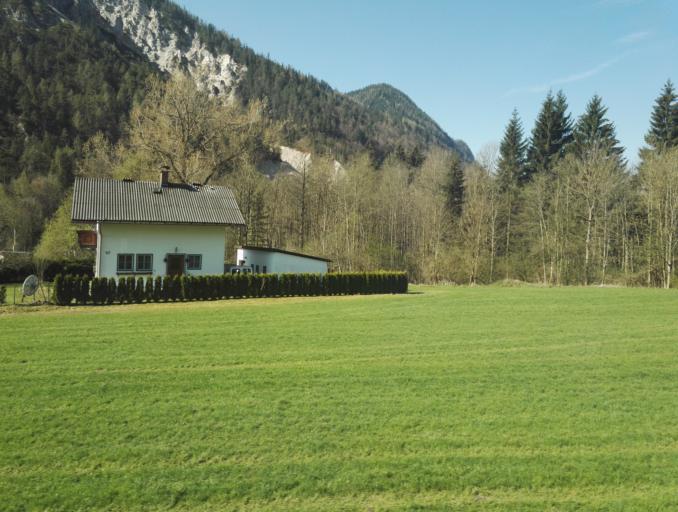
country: AT
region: Salzburg
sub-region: Politischer Bezirk Sankt Johann im Pongau
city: Forstau
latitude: 47.4016
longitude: 13.5794
